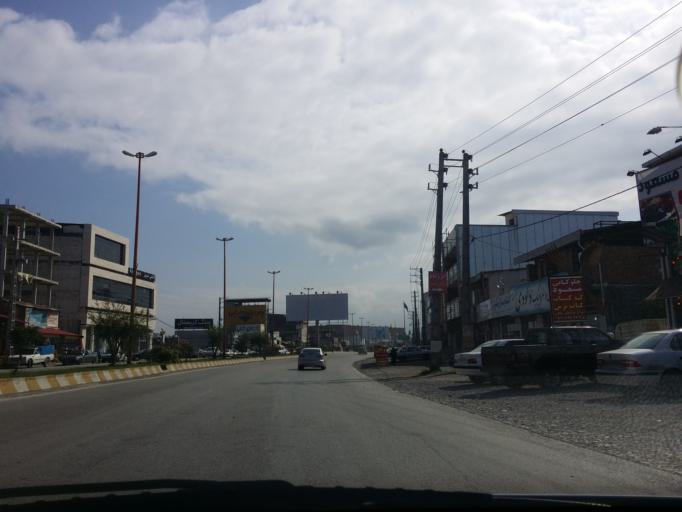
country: IR
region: Mazandaran
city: Chalus
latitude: 36.6853
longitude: 51.3991
